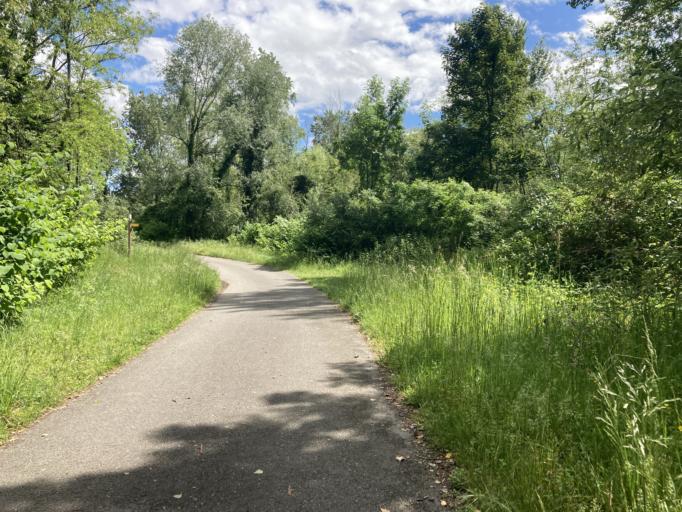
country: FR
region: Aquitaine
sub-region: Departement des Pyrenees-Atlantiques
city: Artiguelouve
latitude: 43.3306
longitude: -0.4668
